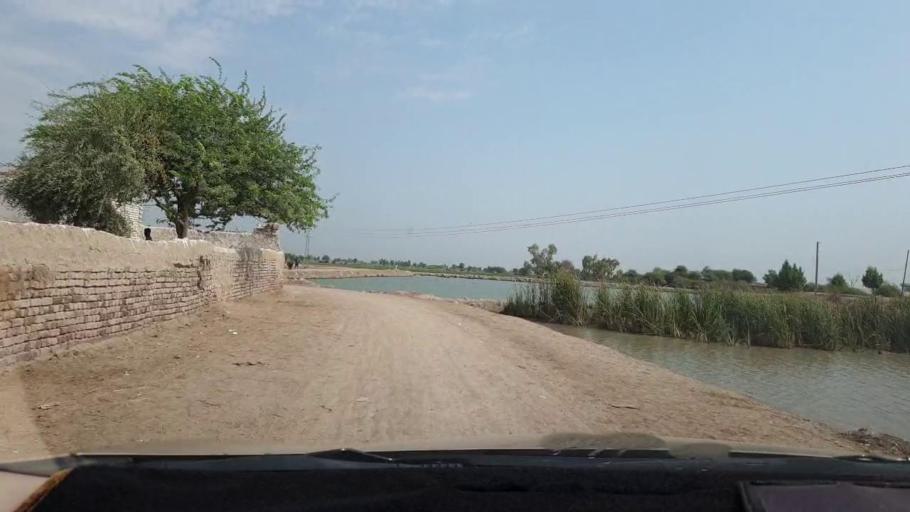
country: PK
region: Sindh
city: Larkana
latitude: 27.6689
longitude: 68.2224
